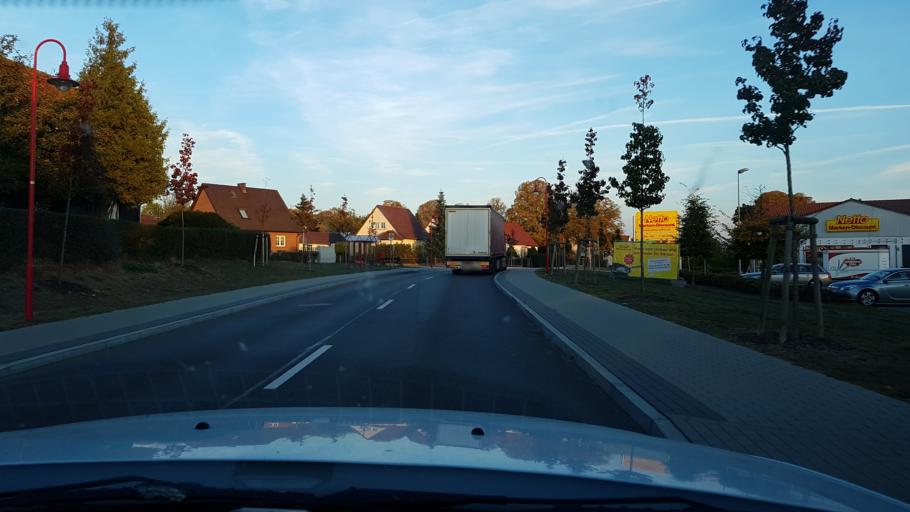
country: DE
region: Brandenburg
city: Gartz
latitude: 53.2120
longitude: 14.3724
